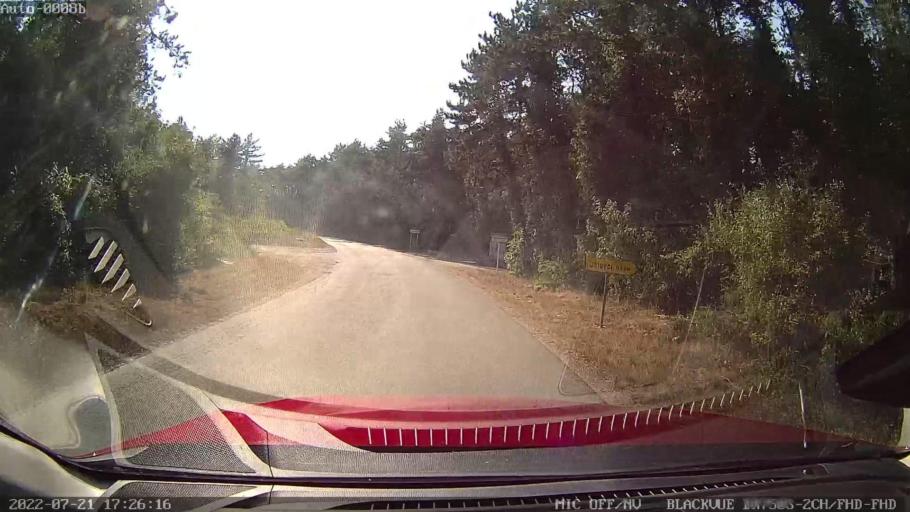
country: HR
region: Istarska
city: Karojba
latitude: 45.1844
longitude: 13.8122
